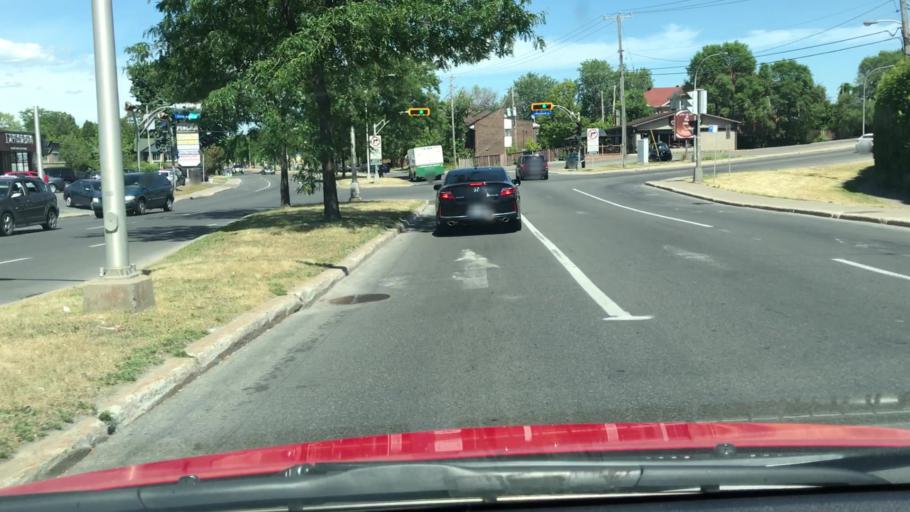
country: CA
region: Quebec
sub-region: Laval
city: Laval
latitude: 45.5294
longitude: -73.7560
